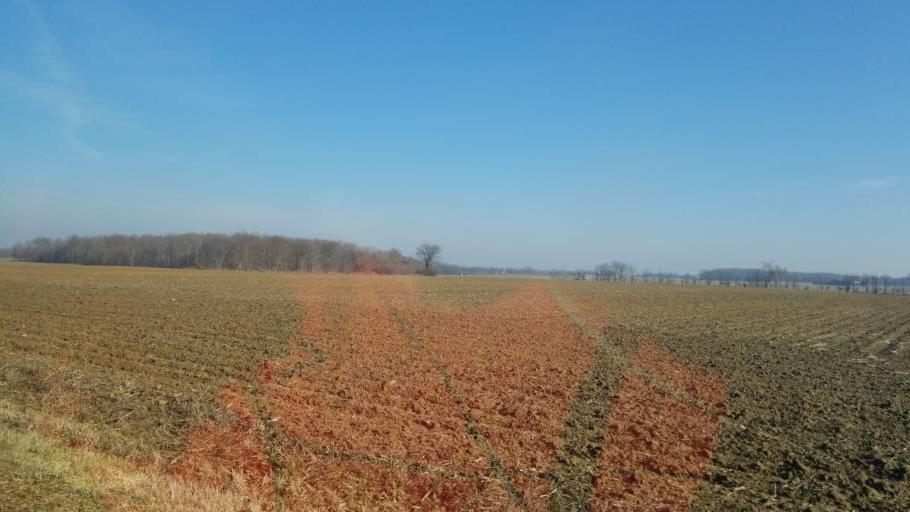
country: US
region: Ohio
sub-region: Seneca County
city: Tiffin
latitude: 41.0246
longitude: -83.0741
